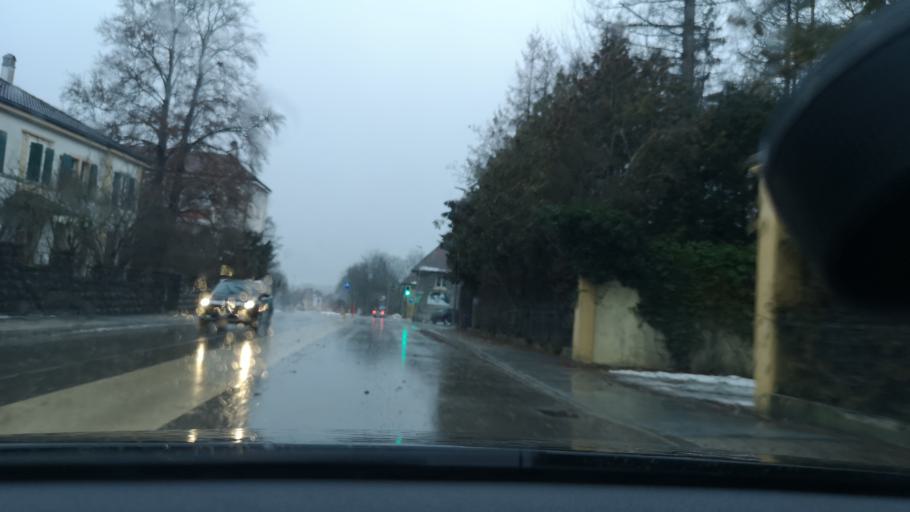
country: CH
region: Neuchatel
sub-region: Val-de-Travers District
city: Couvet
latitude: 46.9272
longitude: 6.6337
